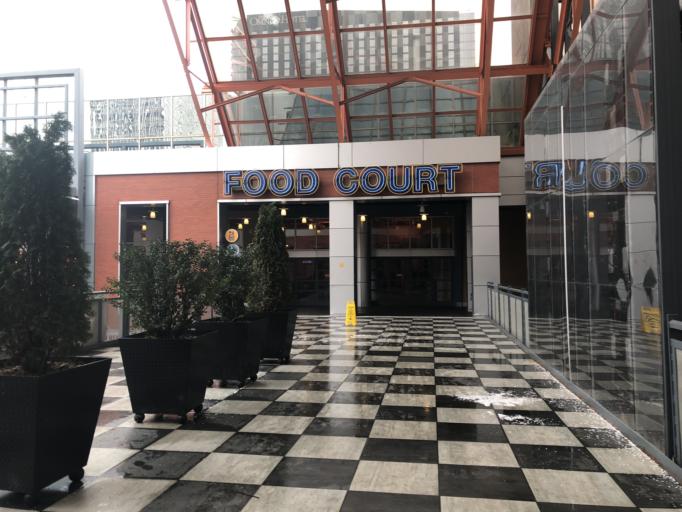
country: US
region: Kentucky
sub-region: Jefferson County
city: Louisville
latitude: 38.2521
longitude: -85.7575
